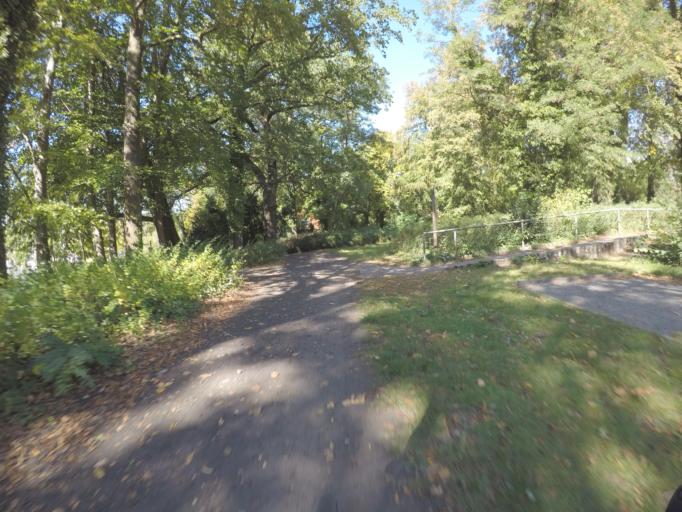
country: DE
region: Berlin
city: Heiligensee
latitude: 52.5924
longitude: 13.2664
